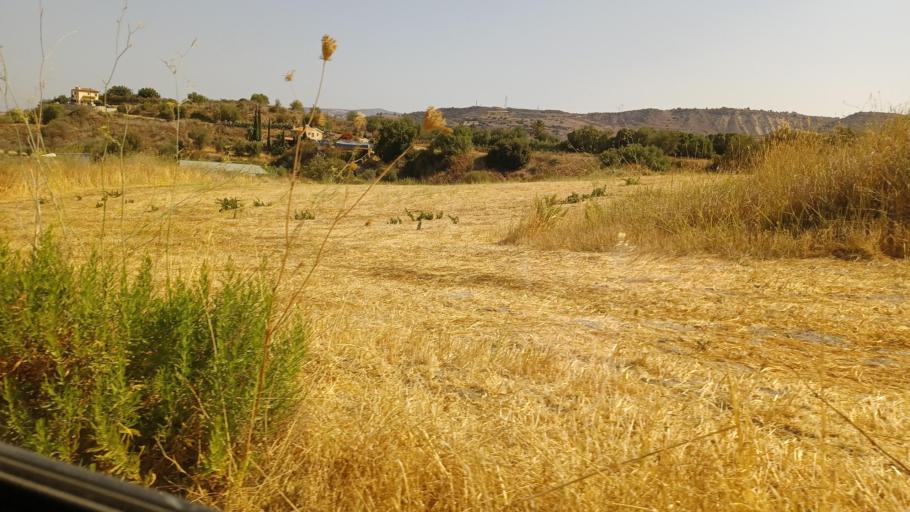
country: CY
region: Pafos
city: Tala
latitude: 34.9100
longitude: 32.4804
